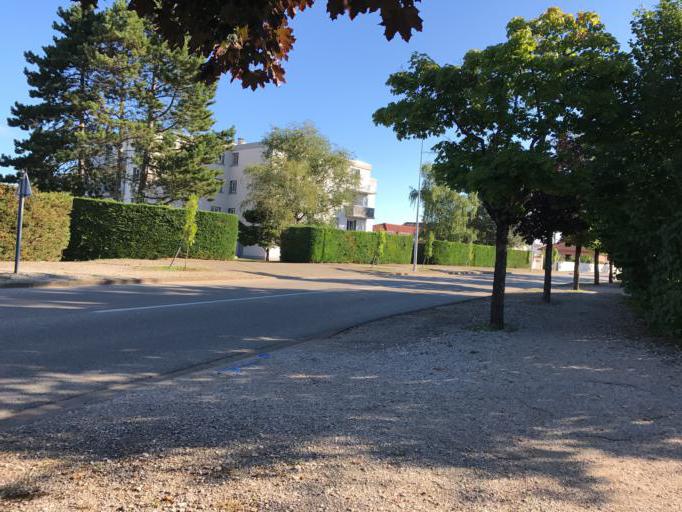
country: FR
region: Rhone-Alpes
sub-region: Departement de l'Ain
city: Amberieu-en-Bugey
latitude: 45.9585
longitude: 5.3455
